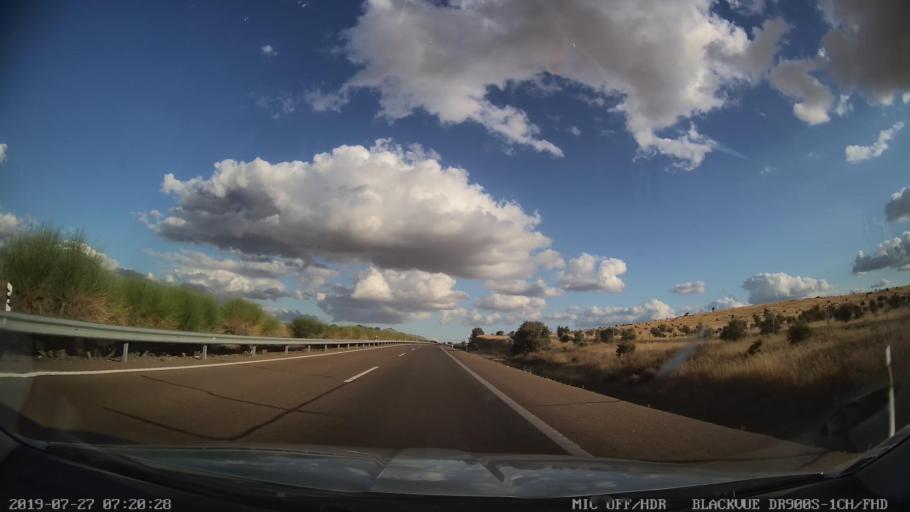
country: ES
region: Extremadura
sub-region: Provincia de Caceres
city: Santa Cruz de la Sierra
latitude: 39.3804
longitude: -5.8815
